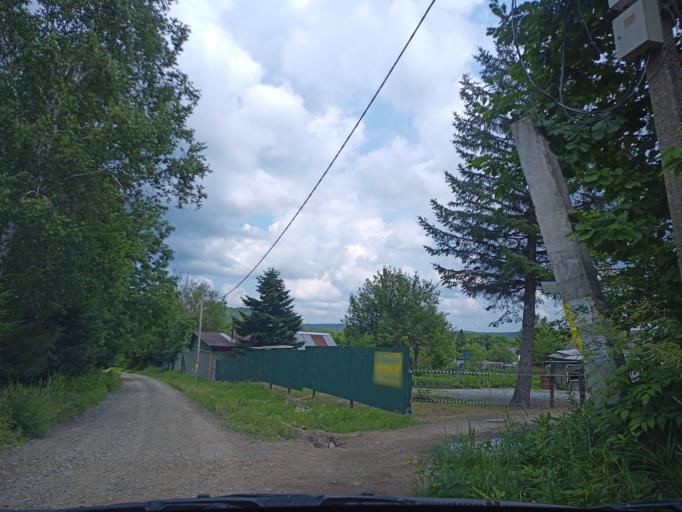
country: RU
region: Khabarovsk Krai
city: Korfovskiy
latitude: 48.3213
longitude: 135.0993
